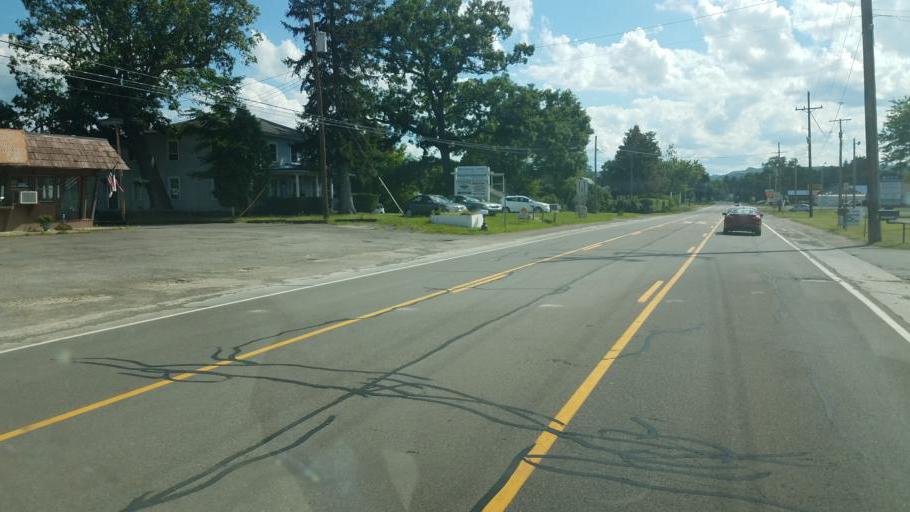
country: US
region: New York
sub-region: Steuben County
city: Bath
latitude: 42.3509
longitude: -77.3059
